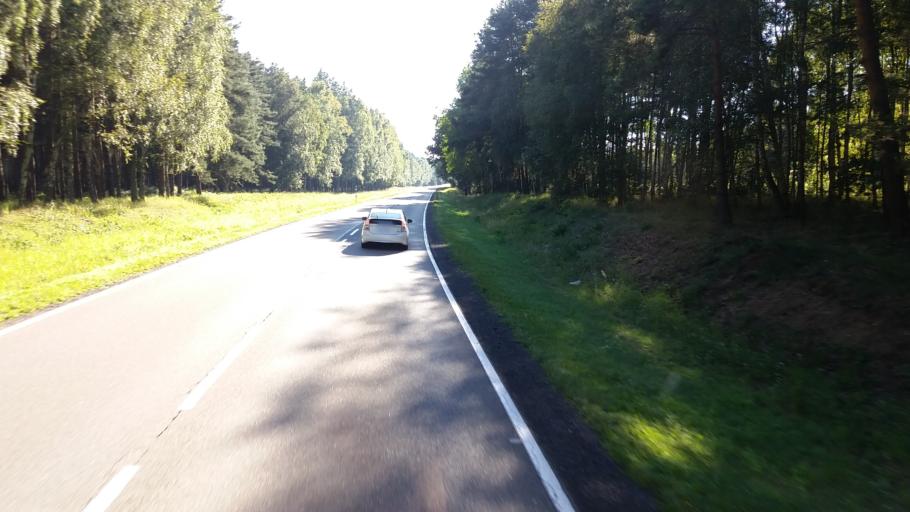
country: PL
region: West Pomeranian Voivodeship
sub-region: Powiat choszczenski
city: Drawno
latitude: 53.2951
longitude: 15.7360
